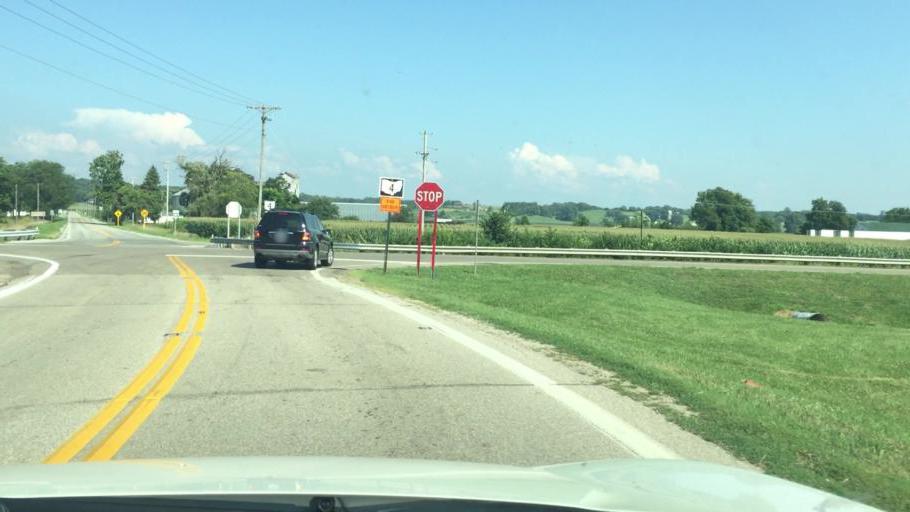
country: US
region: Ohio
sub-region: Champaign County
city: Mechanicsburg
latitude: 40.0301
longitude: -83.6551
